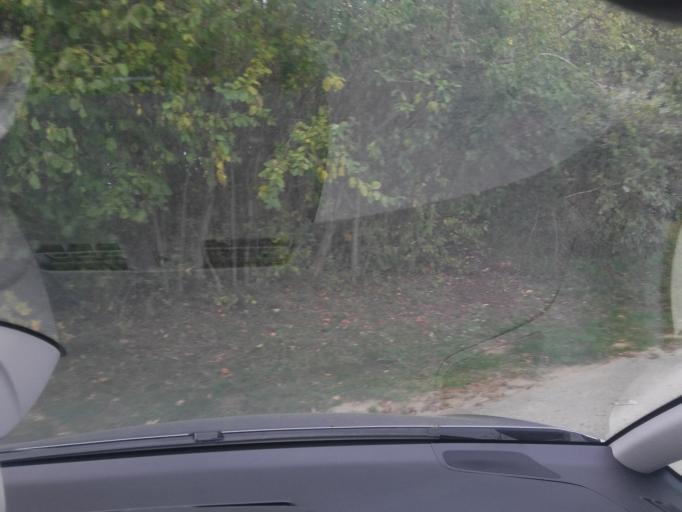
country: BE
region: Wallonia
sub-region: Province du Luxembourg
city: Arlon
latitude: 49.6918
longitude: 5.8227
